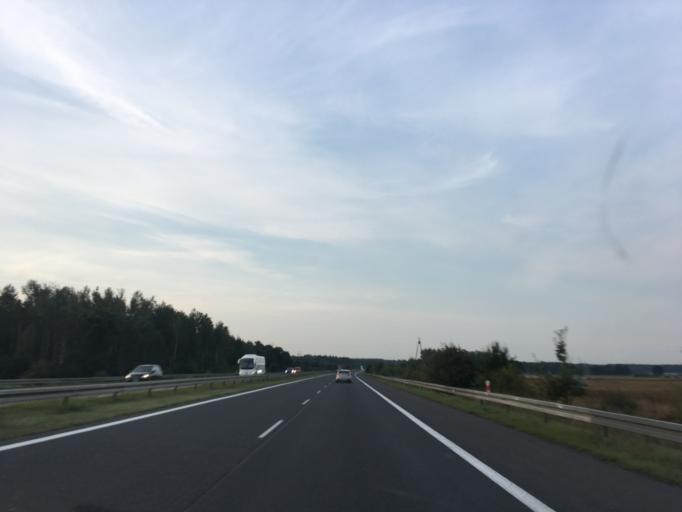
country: PL
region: Lodz Voivodeship
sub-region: Powiat radomszczanski
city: Kamiensk
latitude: 51.2586
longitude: 19.5285
